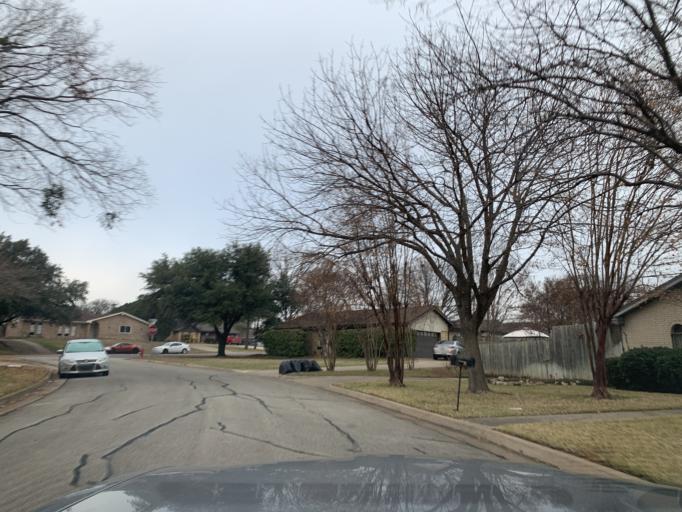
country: US
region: Texas
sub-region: Tarrant County
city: Bedford
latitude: 32.8358
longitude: -97.1535
